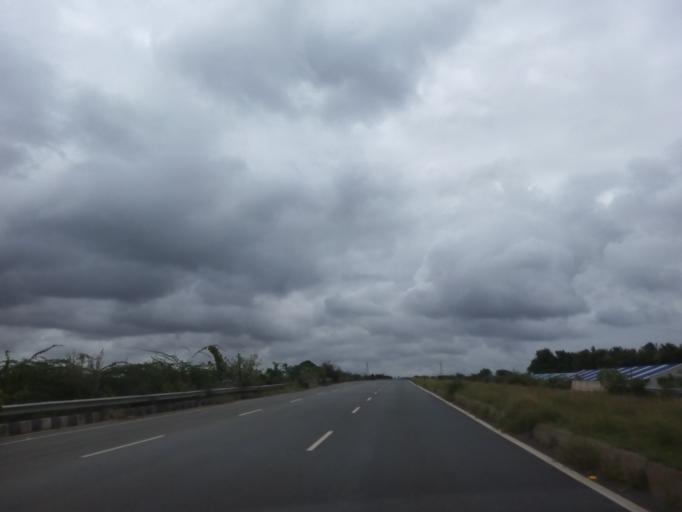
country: IN
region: Karnataka
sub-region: Haveri
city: Haveri
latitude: 14.7749
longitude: 75.4040
